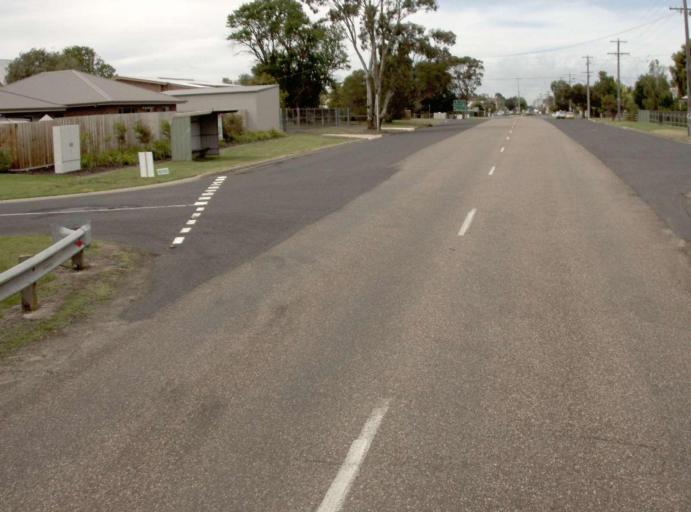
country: AU
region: Victoria
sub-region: Wellington
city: Sale
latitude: -37.9613
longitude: 147.0809
